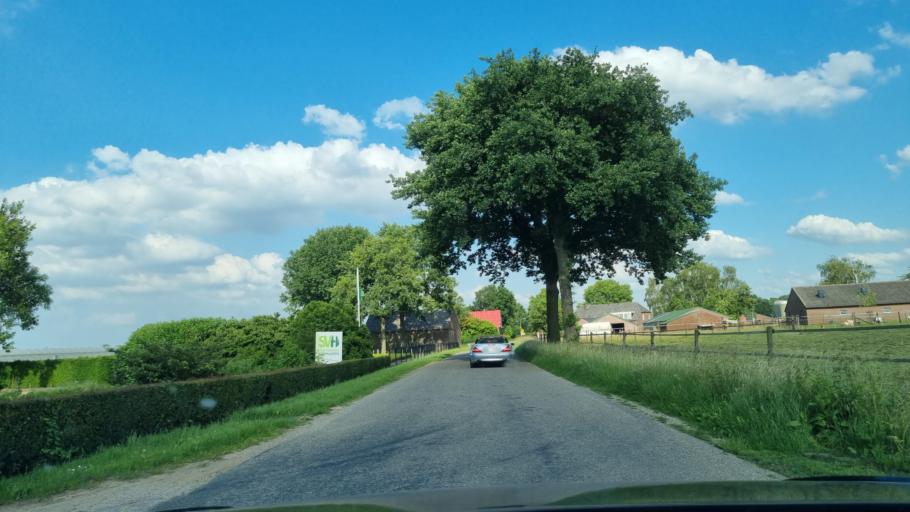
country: NL
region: Limburg
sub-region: Gemeente Gennep
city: Gennep
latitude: 51.7117
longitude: 5.9900
